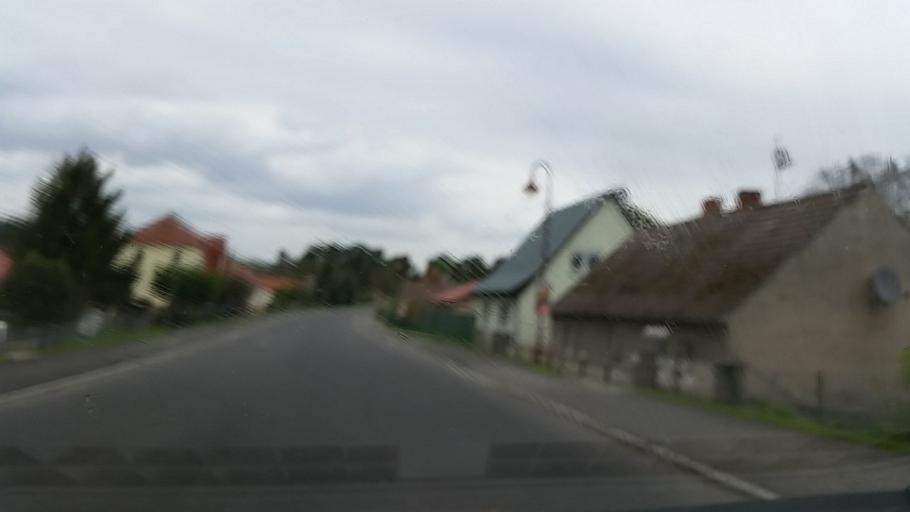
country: DE
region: Brandenburg
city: Reichenwalde
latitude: 52.2920
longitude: 13.9859
